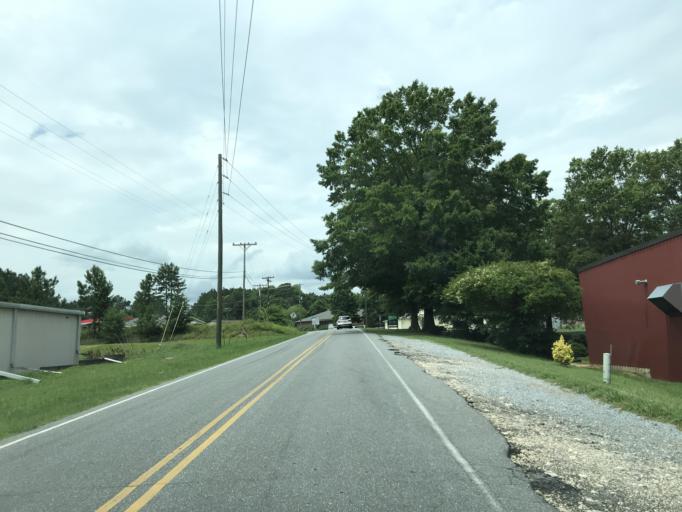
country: US
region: North Carolina
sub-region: Lincoln County
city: Lincolnton
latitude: 35.4876
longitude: -81.2515
